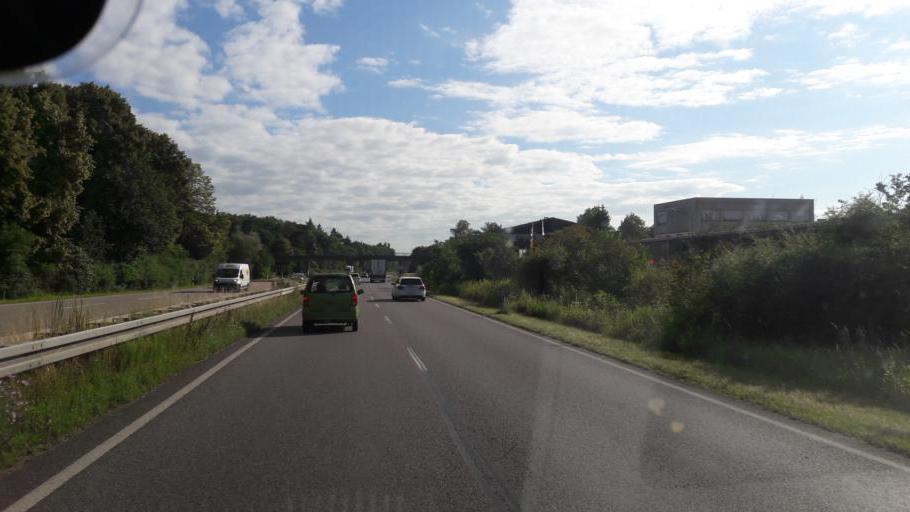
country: DE
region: Baden-Wuerttemberg
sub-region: Karlsruhe Region
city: Ettlingen
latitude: 48.9537
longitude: 8.3728
